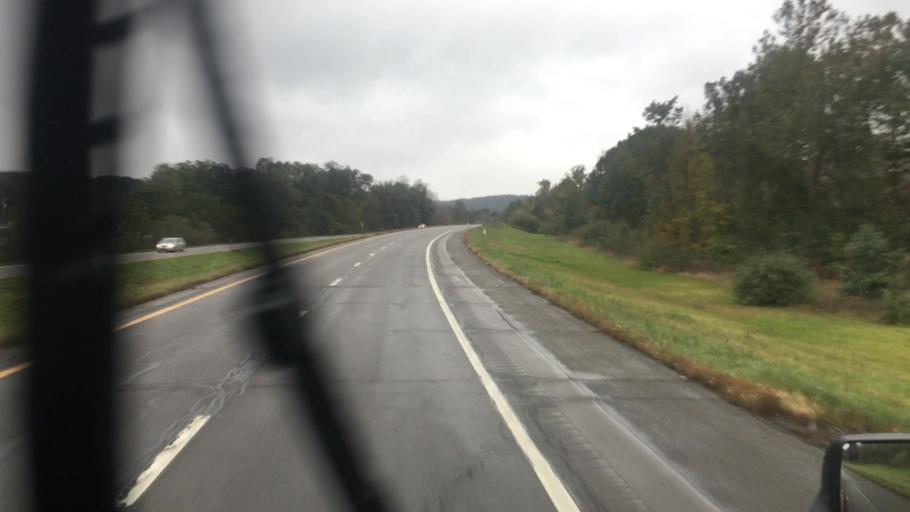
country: US
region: New York
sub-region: Tioga County
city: Apalachin
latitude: 42.0759
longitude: -76.1554
